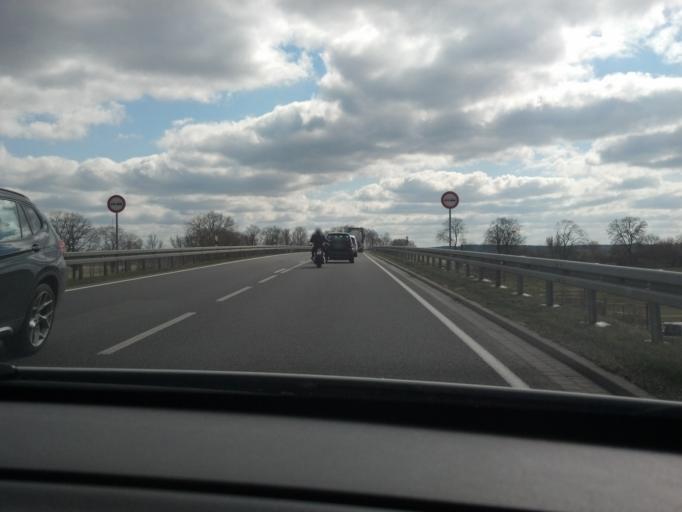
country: DE
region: Mecklenburg-Vorpommern
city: Neustrelitz
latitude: 53.3326
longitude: 13.1095
